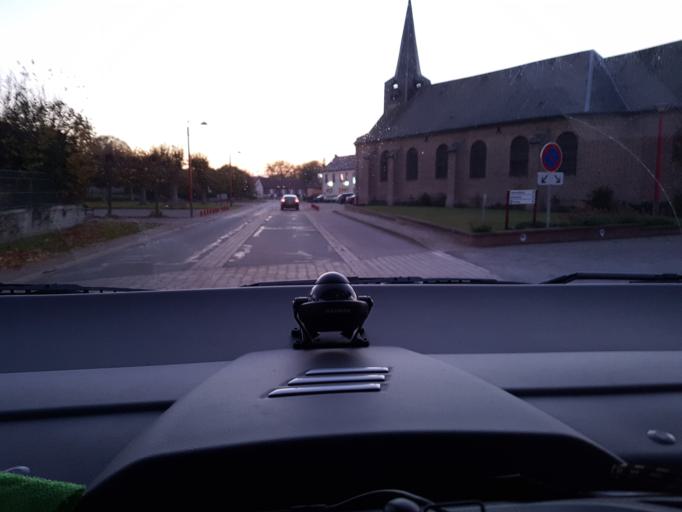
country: FR
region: Picardie
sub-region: Departement de la Somme
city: Sailly-Flibeaucourt
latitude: 50.2160
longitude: 1.7120
